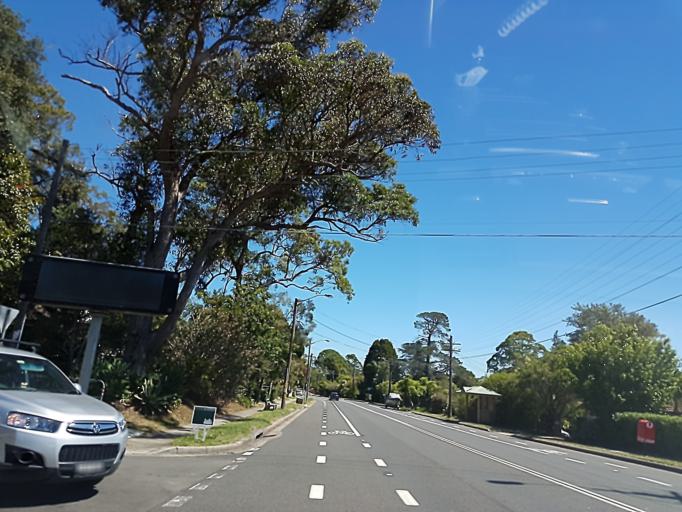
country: AU
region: New South Wales
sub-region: Hornsby Shire
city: Asquith
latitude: -33.6890
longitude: 151.0974
